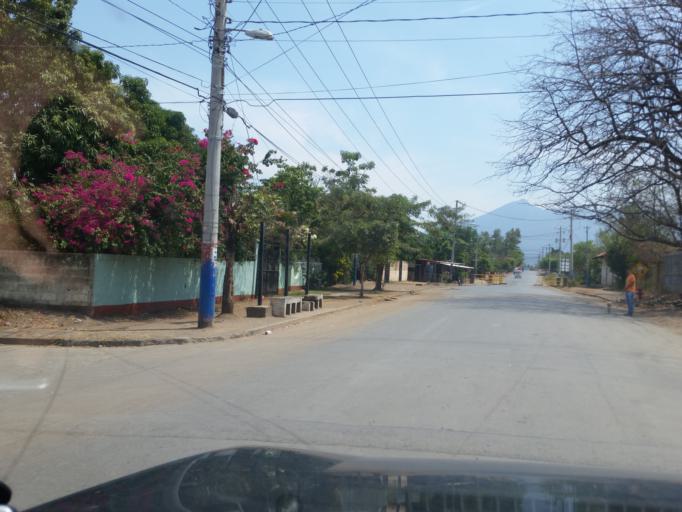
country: NI
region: Granada
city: Granada
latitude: 11.9432
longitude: -85.9621
